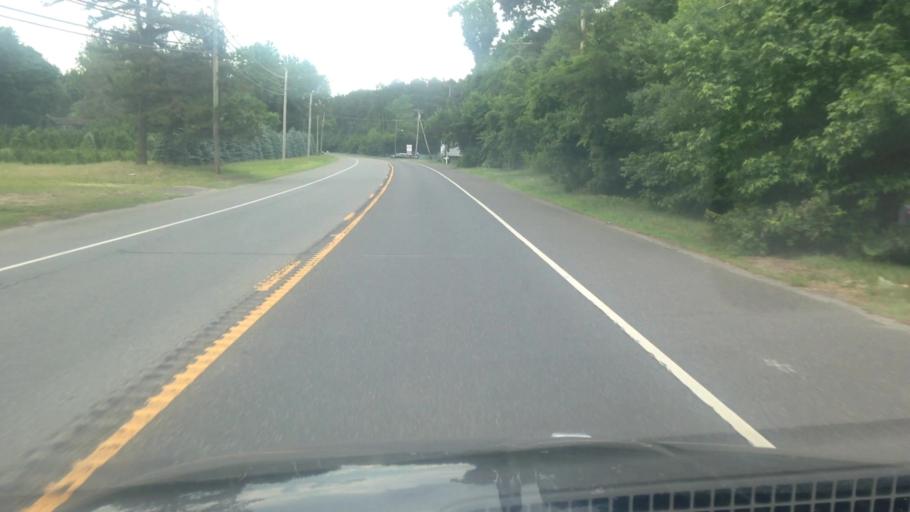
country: US
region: New Jersey
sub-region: Burlington County
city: Leisuretowne
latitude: 39.8407
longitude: -74.7359
